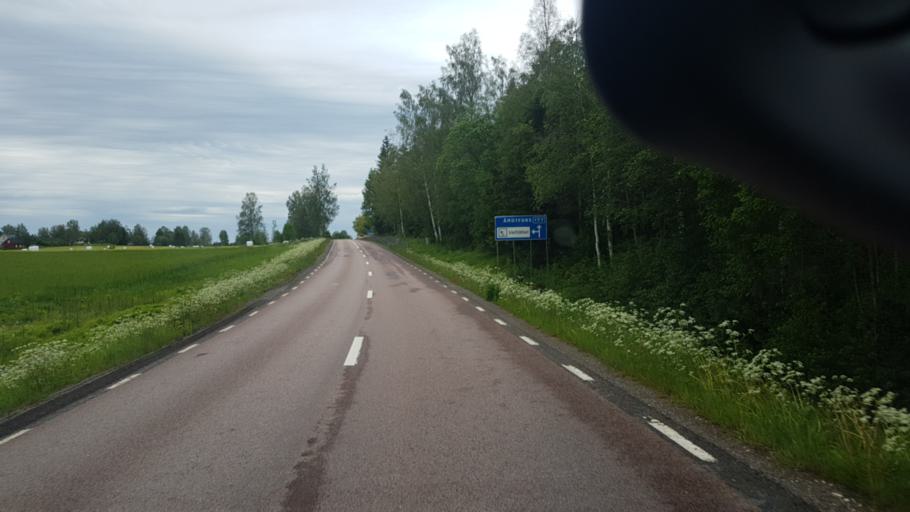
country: SE
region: Vaermland
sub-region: Eda Kommun
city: Amotfors
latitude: 59.7571
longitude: 12.2133
